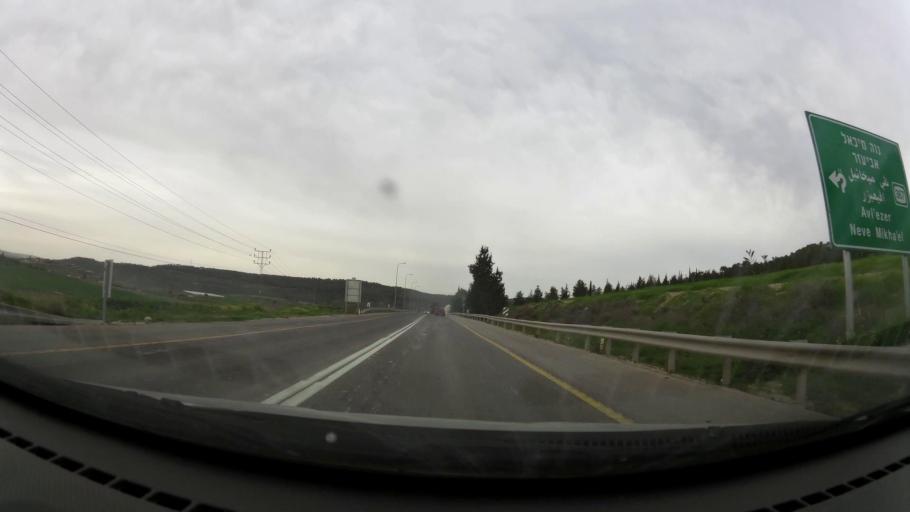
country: IL
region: Jerusalem
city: Bet Shemesh
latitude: 31.6856
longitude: 35.0014
